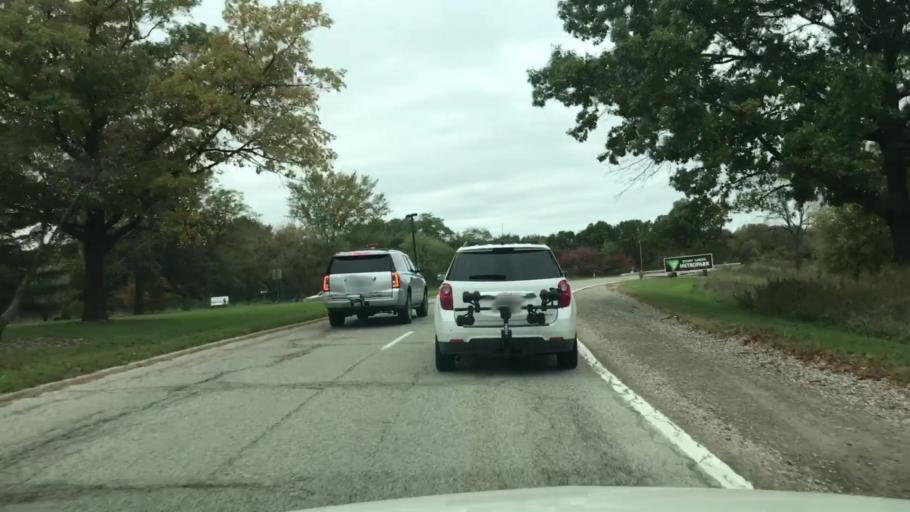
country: US
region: Michigan
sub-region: Macomb County
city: Shelby
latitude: 42.7115
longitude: -83.0713
